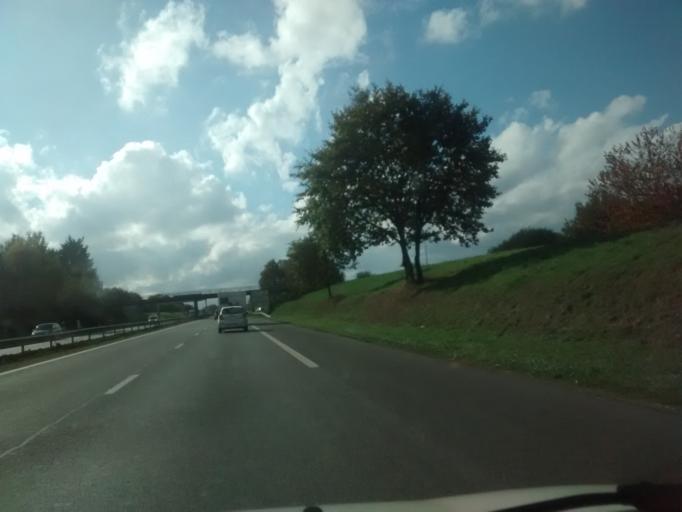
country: FR
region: Brittany
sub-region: Departement d'Ille-et-Vilaine
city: Chantepie
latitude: 48.0972
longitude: -1.6178
